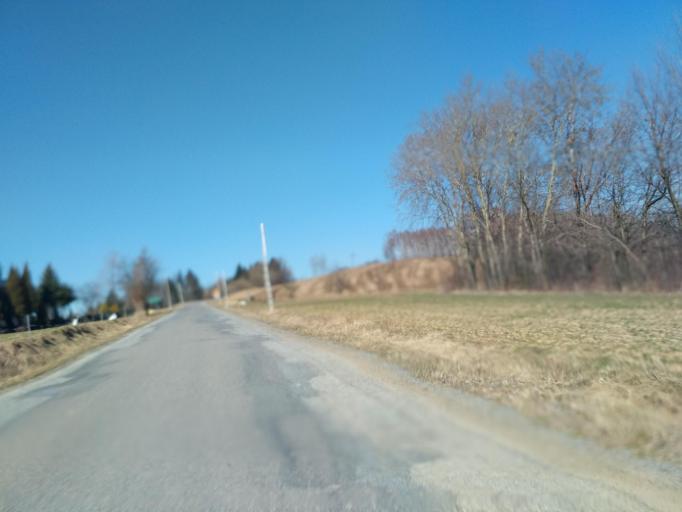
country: PL
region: Subcarpathian Voivodeship
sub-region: Powiat debicki
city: Brzostek
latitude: 49.9461
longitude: 21.4314
